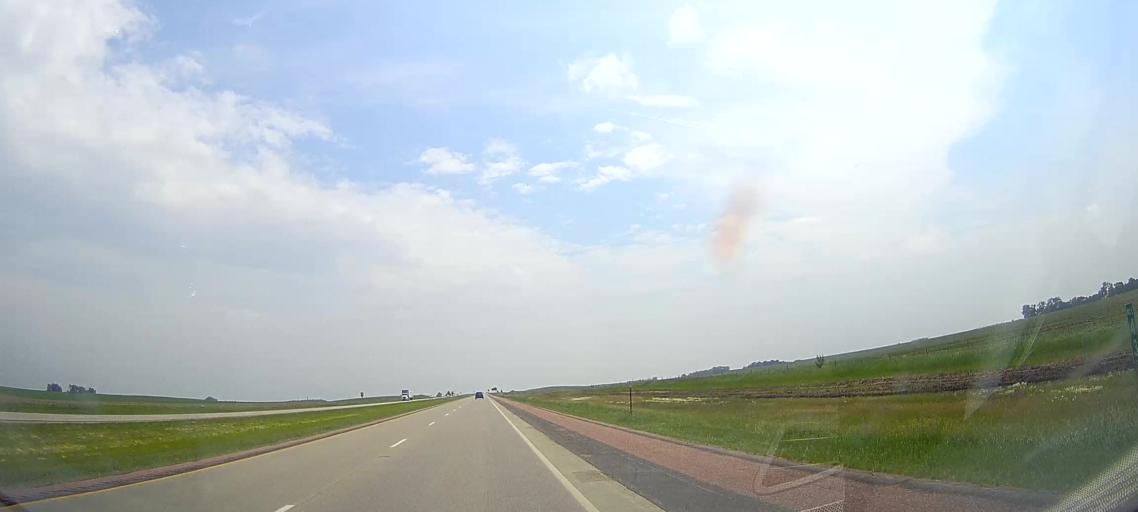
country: US
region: South Dakota
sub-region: Union County
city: Beresford
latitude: 43.0210
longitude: -96.7959
